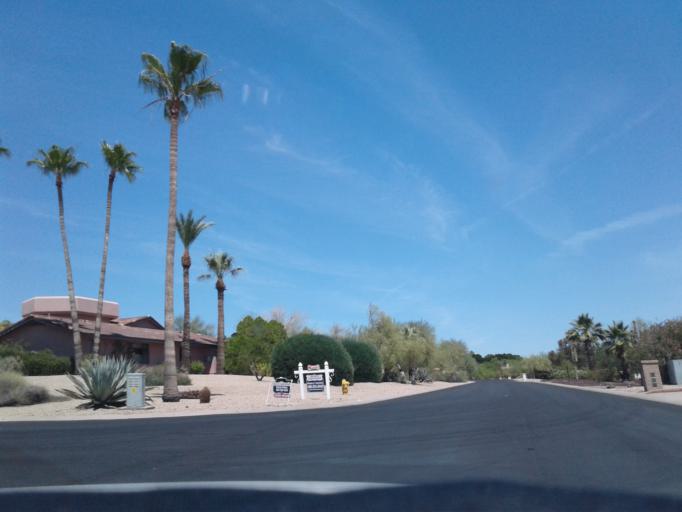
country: US
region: Arizona
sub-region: Maricopa County
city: Paradise Valley
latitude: 33.5303
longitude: -112.0086
